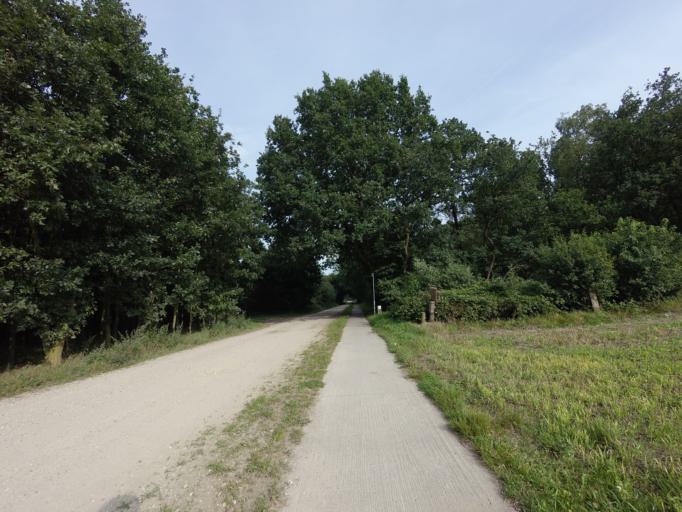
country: DE
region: Lower Saxony
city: Getelo
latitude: 52.4518
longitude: 6.8277
